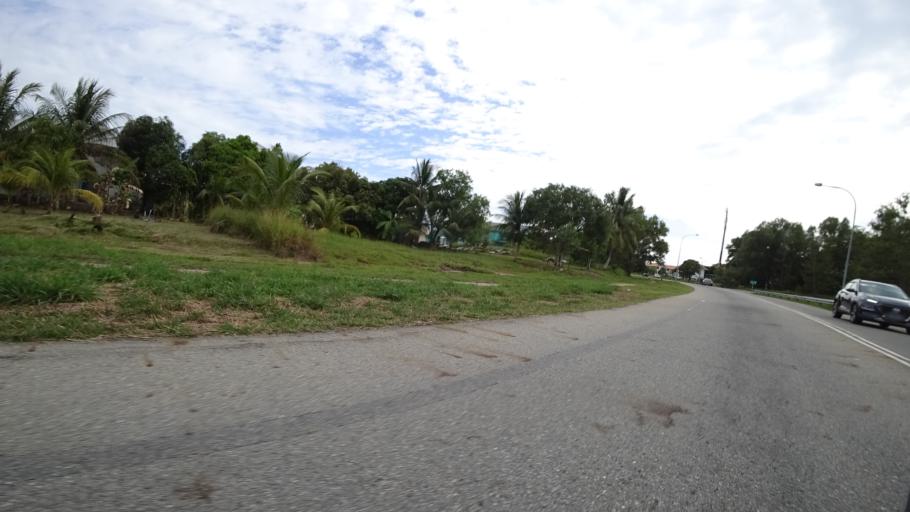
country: BN
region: Brunei and Muara
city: Bandar Seri Begawan
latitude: 4.9646
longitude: 114.9136
